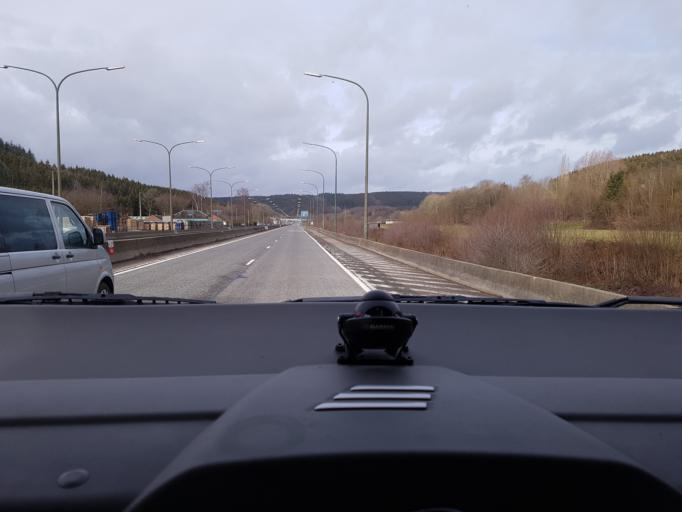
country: BE
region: Wallonia
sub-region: Province du Luxembourg
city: Nassogne
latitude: 50.1543
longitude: 5.4172
